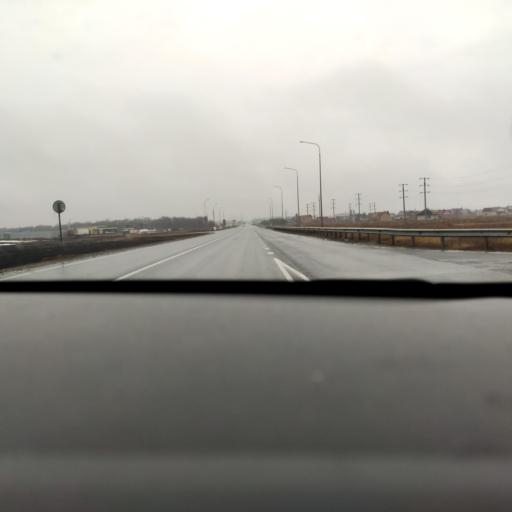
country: RU
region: Tatarstan
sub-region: Alekseyevskiy Rayon
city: Alekseyevskoye
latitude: 55.3088
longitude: 50.1565
